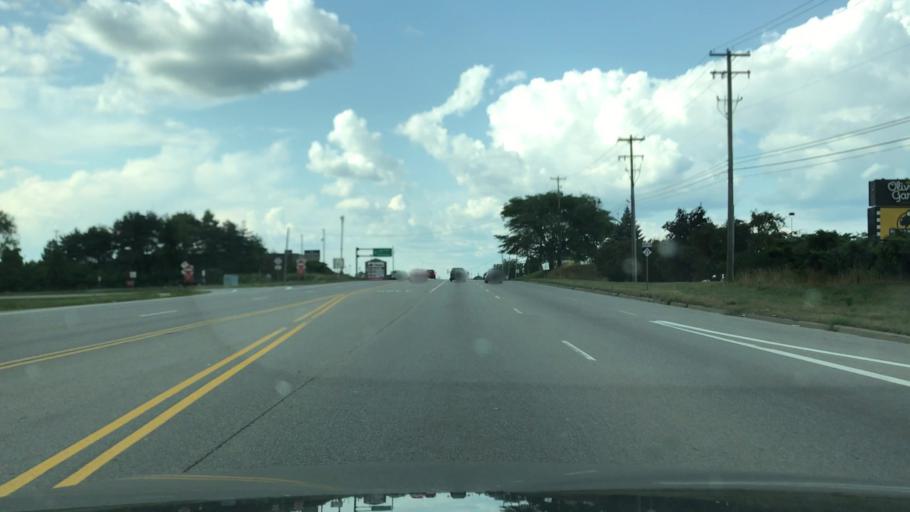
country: US
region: Michigan
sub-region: Kent County
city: Comstock Park
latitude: 43.0182
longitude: -85.6889
